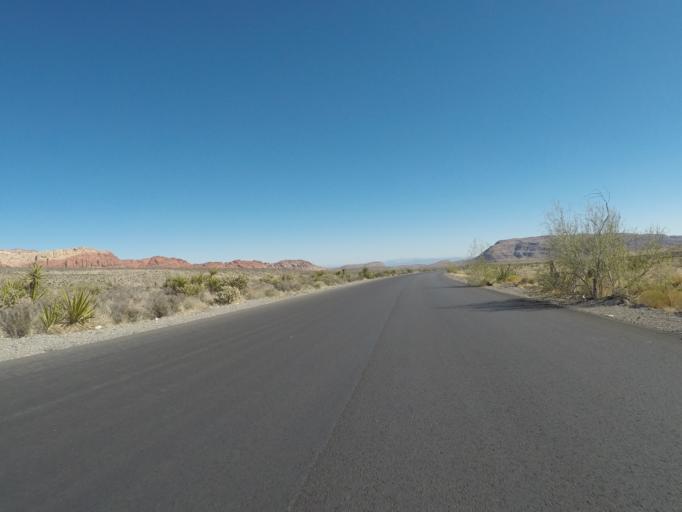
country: US
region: Nevada
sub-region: Clark County
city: Summerlin South
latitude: 36.1420
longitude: -115.4709
